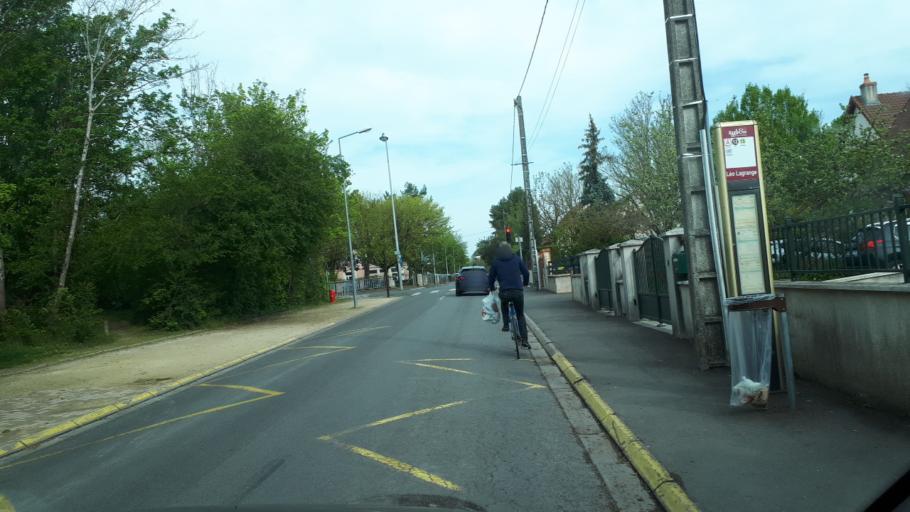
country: FR
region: Centre
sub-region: Departement du Cher
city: Bourges
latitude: 47.0671
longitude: 2.4136
